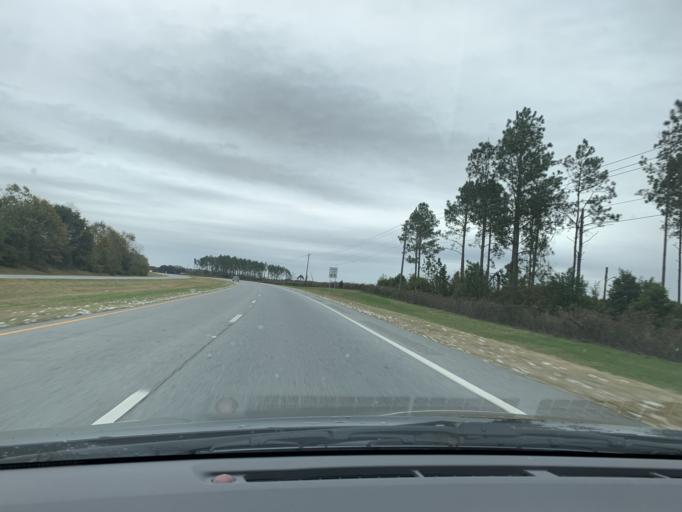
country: US
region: Georgia
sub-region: Seminole County
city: Donalsonville
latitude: 31.0106
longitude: -84.8131
